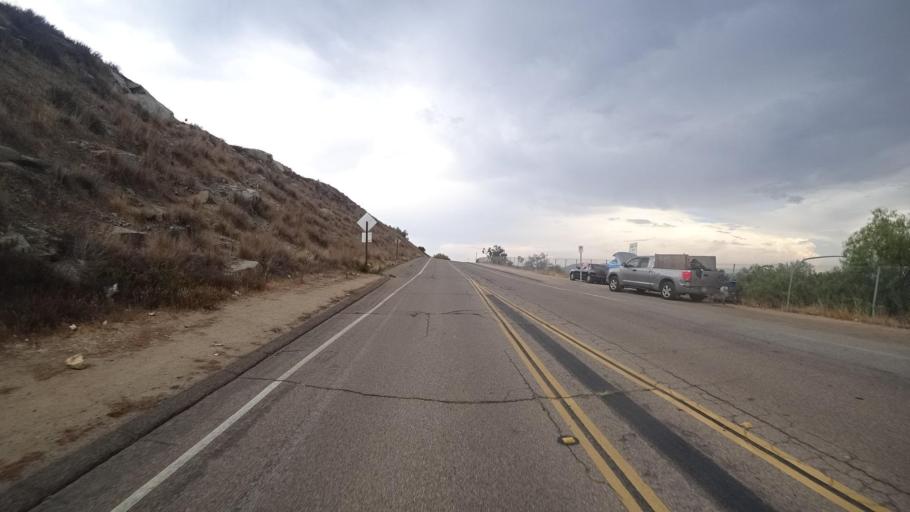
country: US
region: California
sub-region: San Diego County
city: Escondido
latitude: 33.1298
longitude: -117.1063
